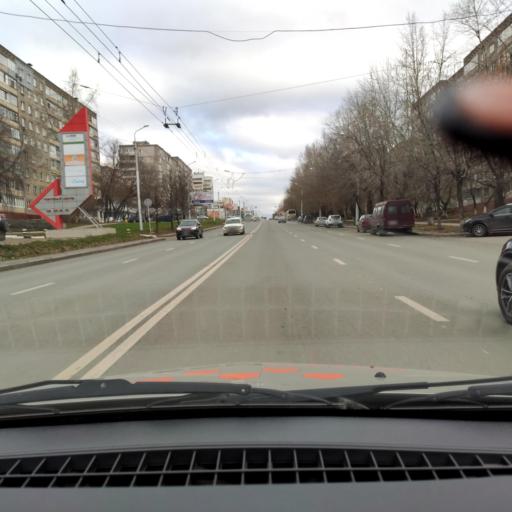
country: RU
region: Bashkortostan
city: Ufa
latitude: 54.7006
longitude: 55.9956
